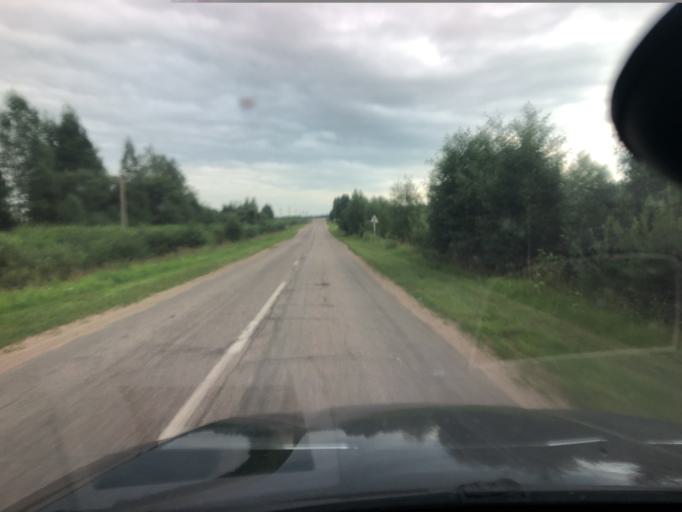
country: RU
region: Jaroslavl
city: Pereslavl'-Zalesskiy
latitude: 57.0243
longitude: 38.9365
